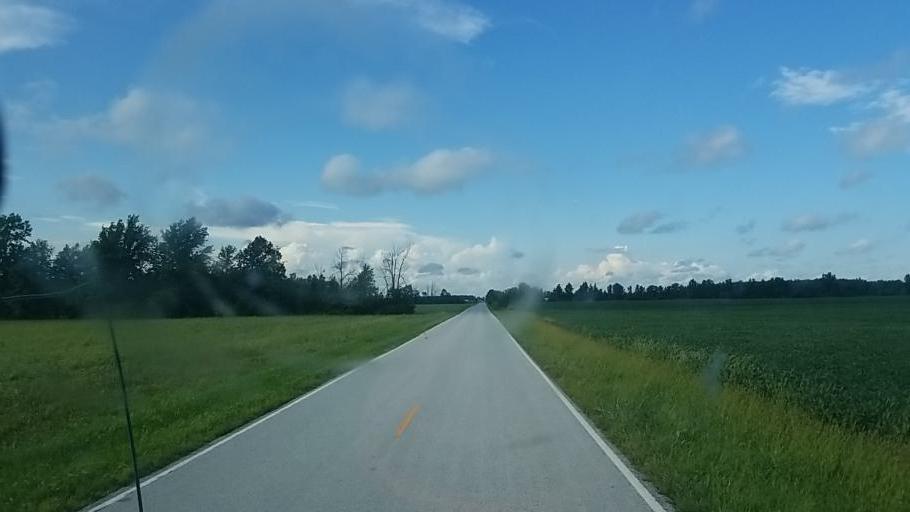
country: US
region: Ohio
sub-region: Hardin County
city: Forest
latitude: 40.7475
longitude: -83.4966
